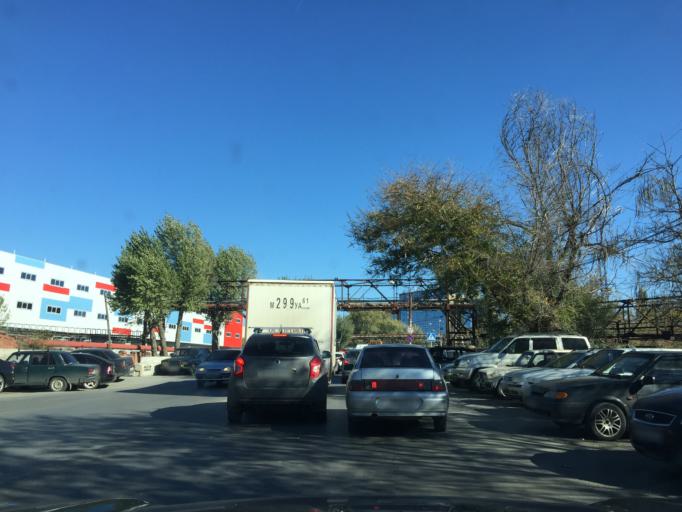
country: RU
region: Rostov
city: Imeni Chkalova
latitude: 47.2670
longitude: 39.7574
